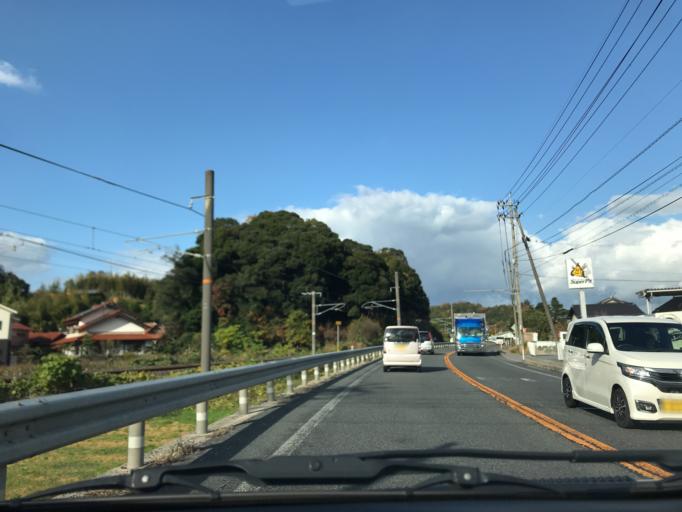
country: JP
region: Shimane
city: Yasugicho
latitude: 35.4255
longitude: 133.2764
